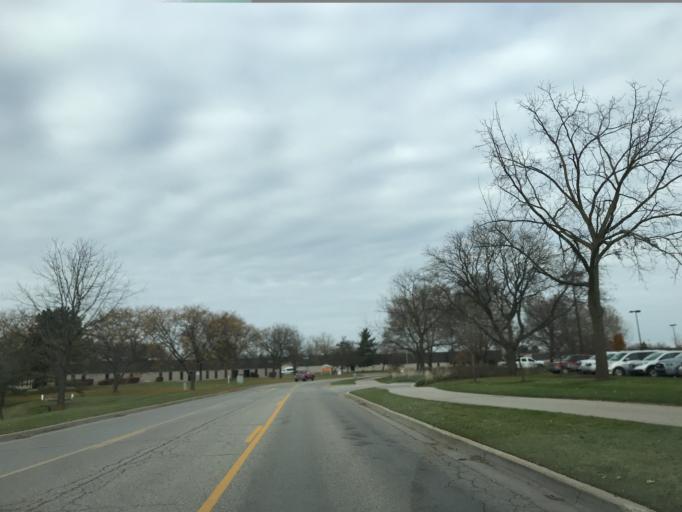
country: US
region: Michigan
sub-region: Washtenaw County
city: Ann Arbor
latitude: 42.2304
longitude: -83.7455
